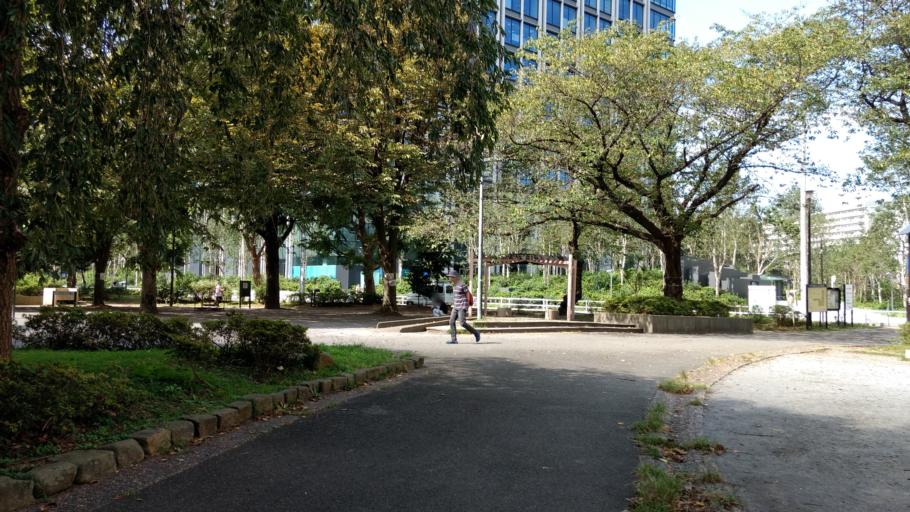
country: JP
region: Tokyo
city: Tokyo
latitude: 35.7081
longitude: 139.7046
